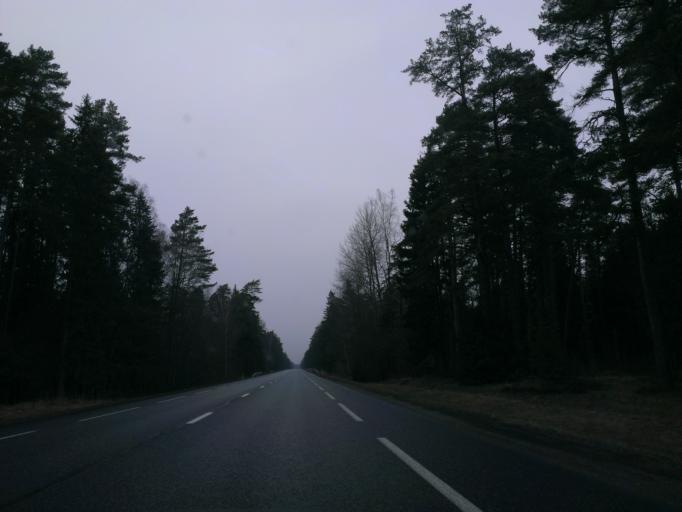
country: LV
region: Saulkrastu
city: Saulkrasti
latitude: 57.4792
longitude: 24.4336
